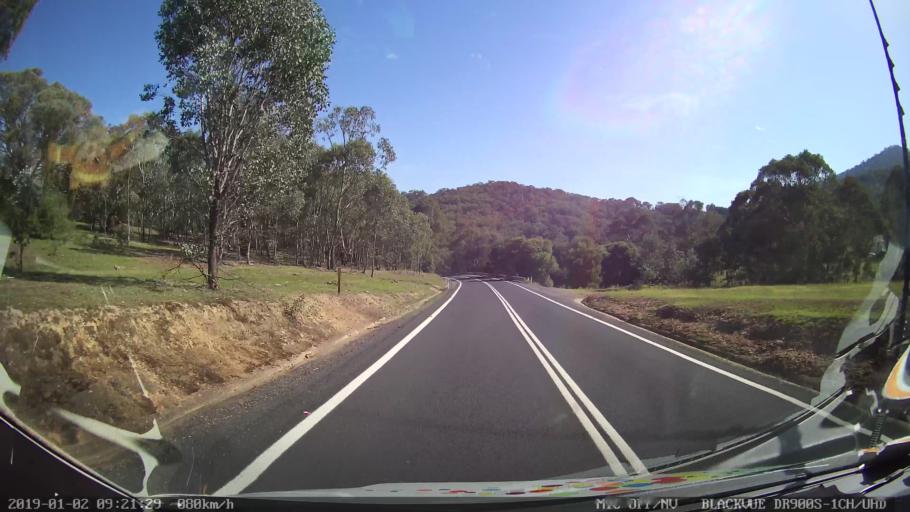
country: AU
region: New South Wales
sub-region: Tumut Shire
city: Tumut
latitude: -35.4052
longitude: 148.2914
